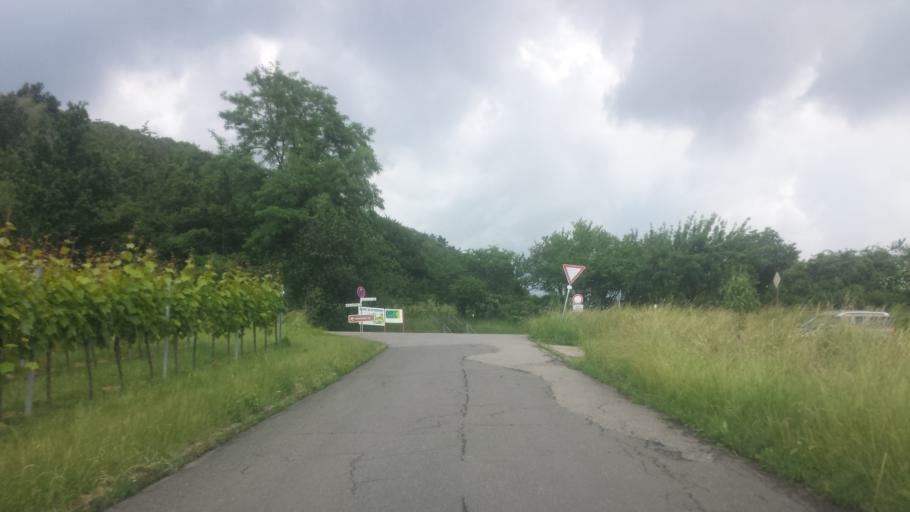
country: DE
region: Rheinland-Pfalz
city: Rhodt unter Rietburg
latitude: 49.2824
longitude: 8.0973
